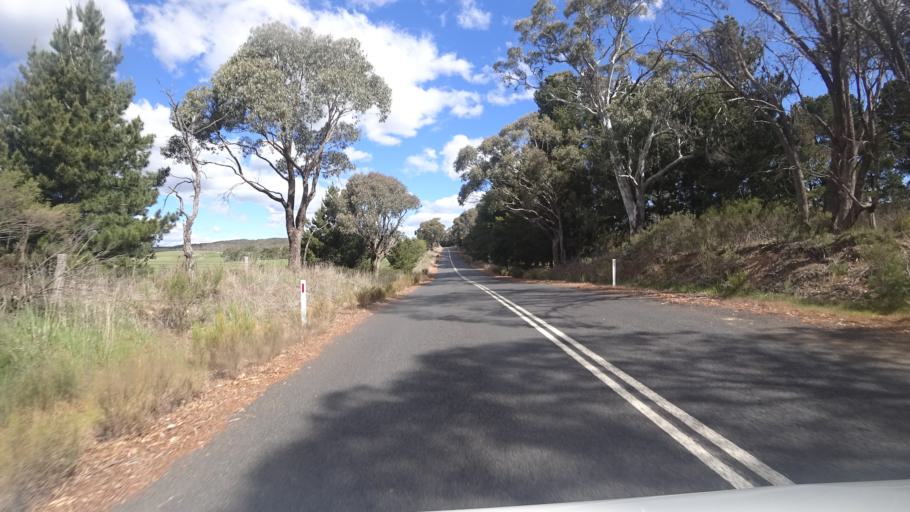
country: AU
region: New South Wales
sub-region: Oberon
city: Oberon
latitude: -33.6732
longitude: 149.7847
